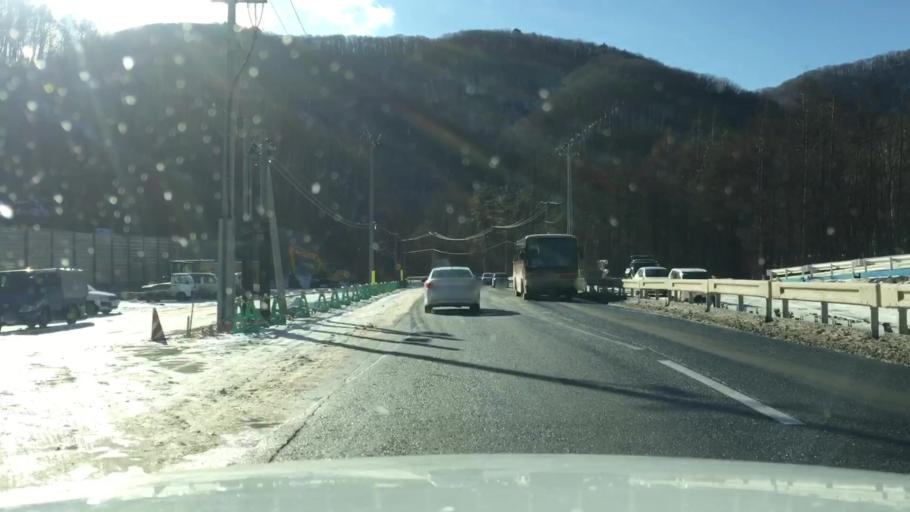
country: JP
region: Iwate
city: Morioka-shi
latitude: 39.6298
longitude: 141.4611
